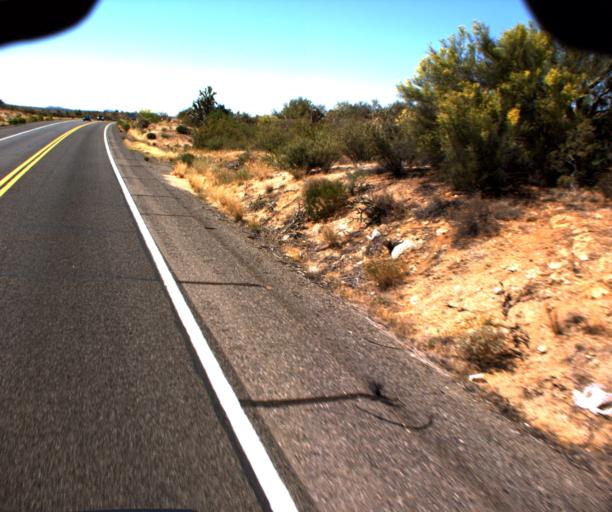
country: US
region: Arizona
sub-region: Yavapai County
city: Congress
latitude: 34.2303
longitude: -113.0705
